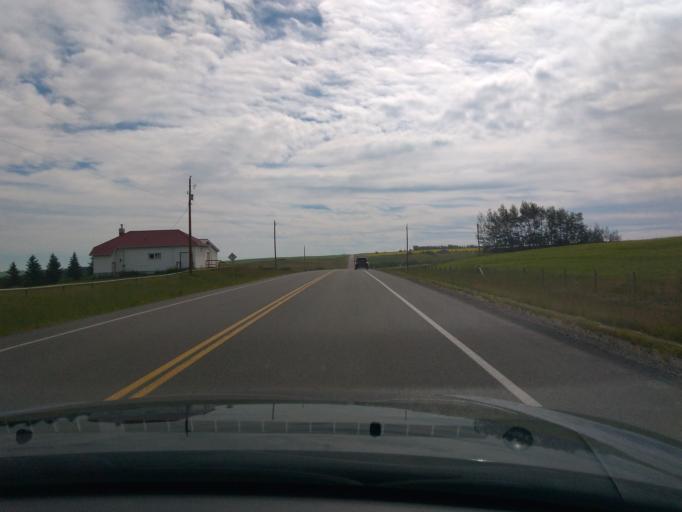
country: CA
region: Alberta
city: Cochrane
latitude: 51.4747
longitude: -114.4256
